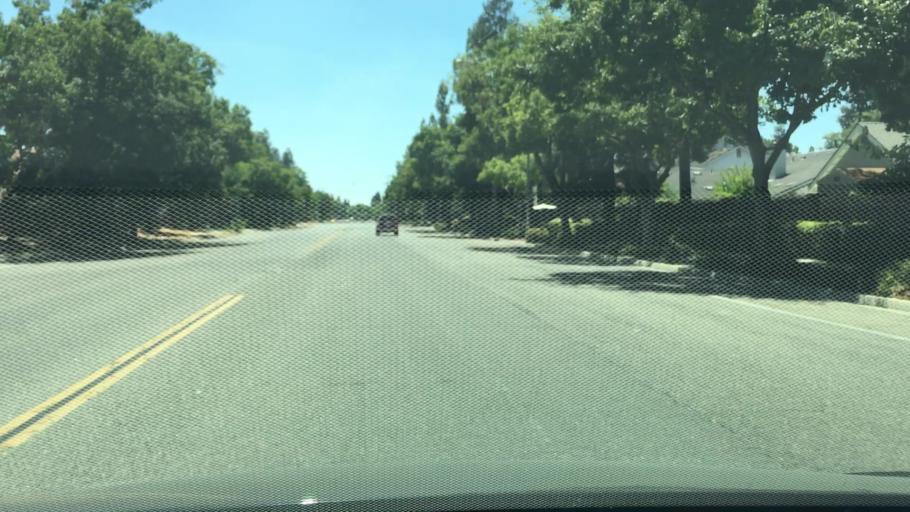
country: US
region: California
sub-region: Fresno County
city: Clovis
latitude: 36.8497
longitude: -119.7478
